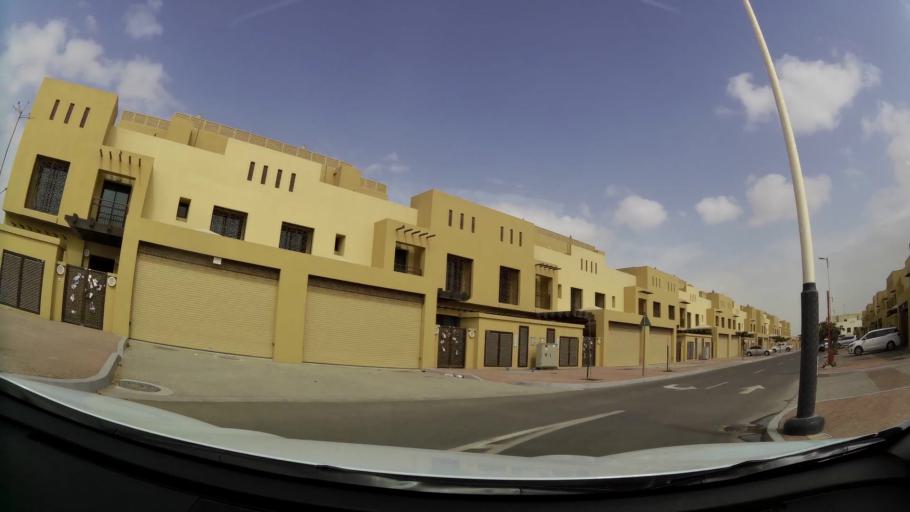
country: AE
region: Abu Dhabi
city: Abu Dhabi
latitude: 24.3998
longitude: 54.4872
